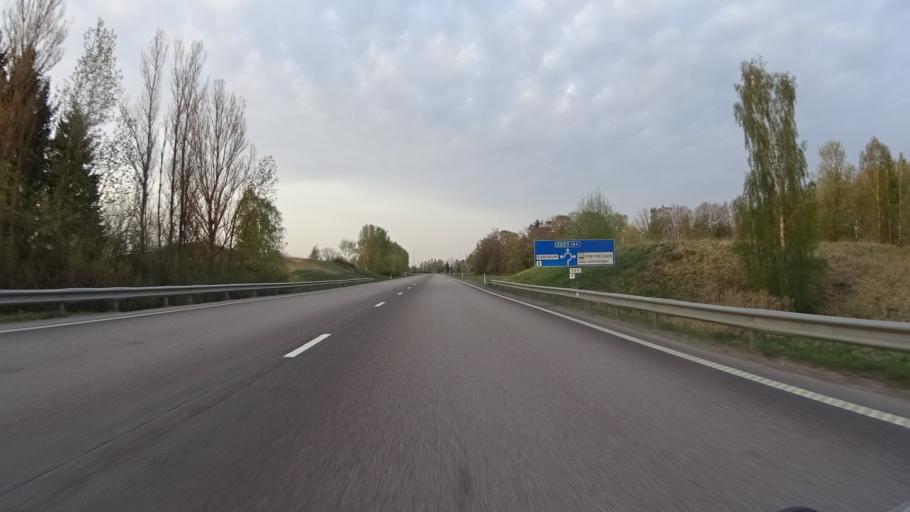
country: SE
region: Vaestra Goetaland
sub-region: Skara Kommun
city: Skara
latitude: 58.3868
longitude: 13.4111
